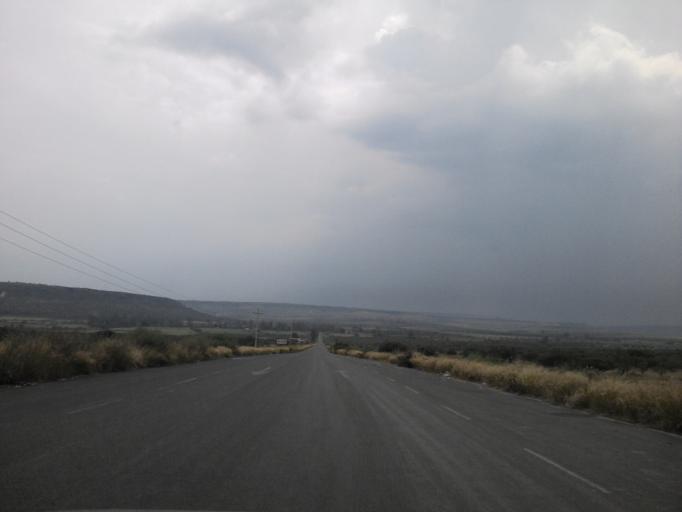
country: MX
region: Jalisco
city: San Diego de Alejandria
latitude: 20.9052
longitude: -102.0478
